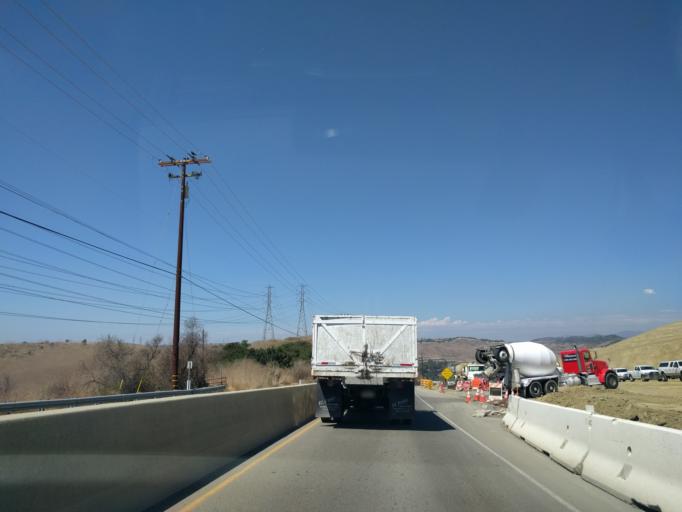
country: US
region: California
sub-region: Orange County
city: San Juan Capistrano
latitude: 33.5074
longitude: -117.6218
